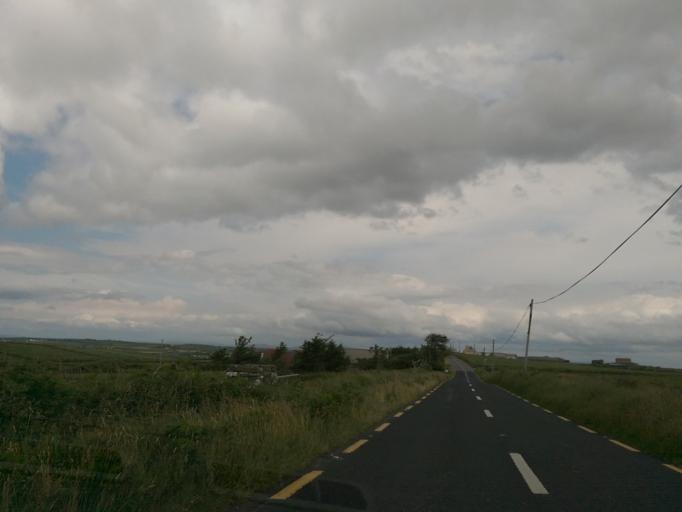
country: IE
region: Munster
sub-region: An Clar
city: Kilrush
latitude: 52.7038
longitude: -9.6129
